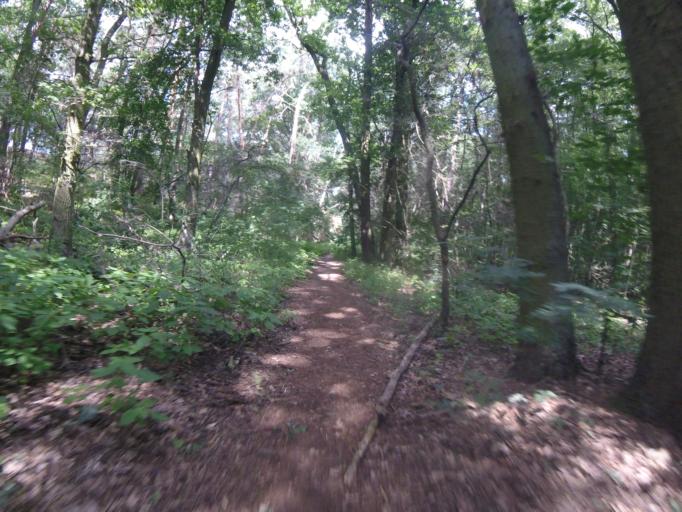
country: DE
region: Brandenburg
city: Bestensee
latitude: 52.2546
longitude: 13.6069
